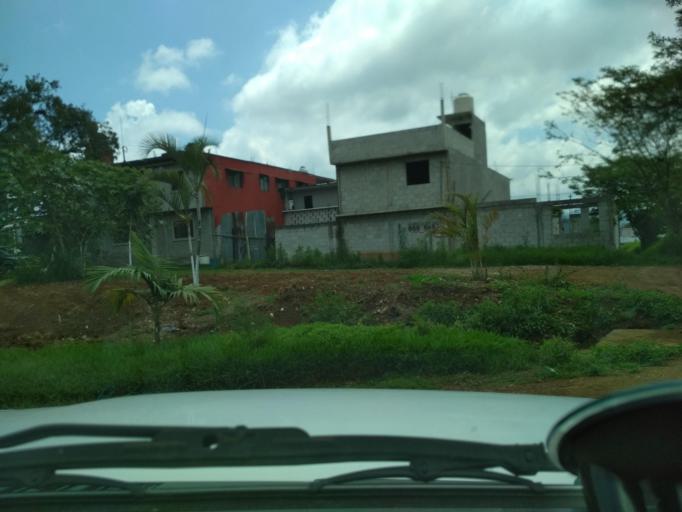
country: MX
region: Veracruz
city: Tocuila
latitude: 18.9536
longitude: -97.0190
